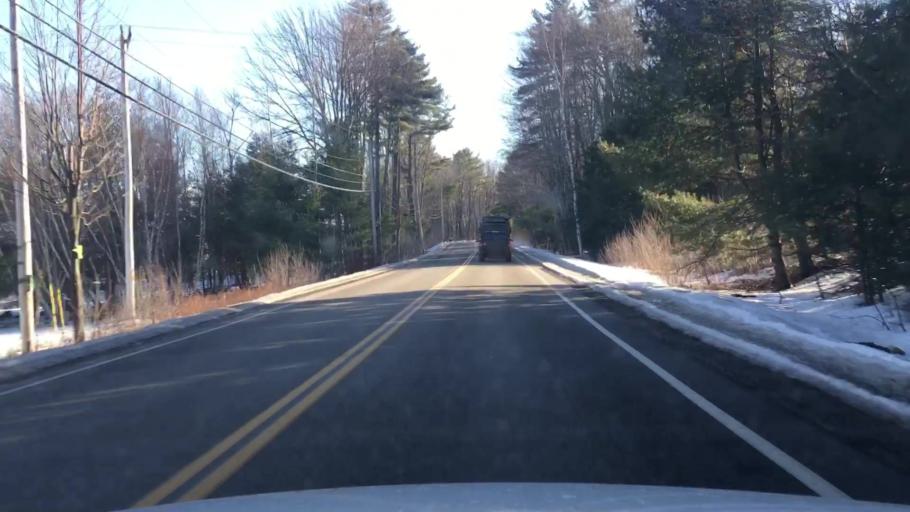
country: US
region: Maine
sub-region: Cumberland County
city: Westbrook
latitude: 43.7006
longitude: -70.3573
